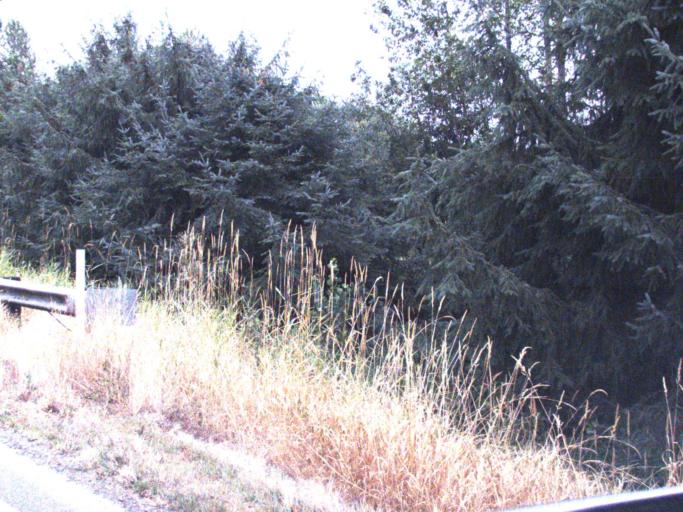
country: US
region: Washington
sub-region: King County
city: Duvall
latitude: 47.7561
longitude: -121.9761
